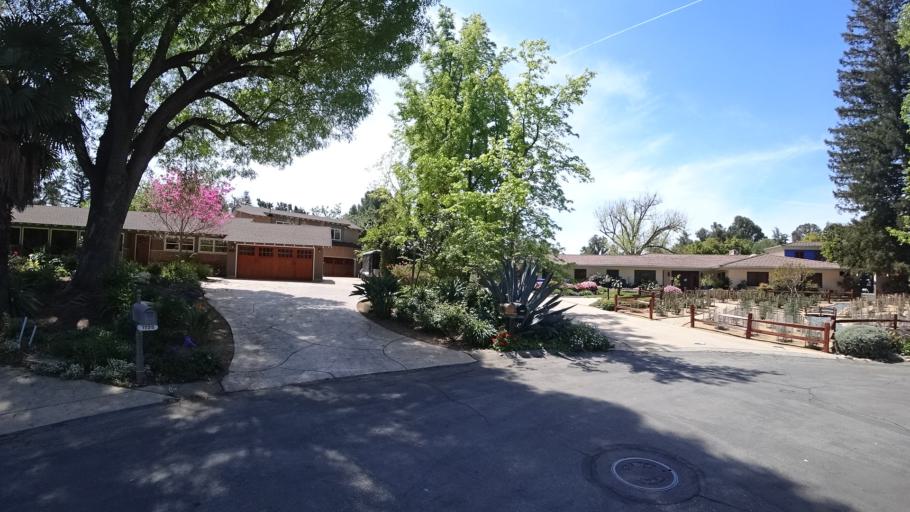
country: US
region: California
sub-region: Ventura County
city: Thousand Oaks
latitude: 34.1934
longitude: -118.8553
